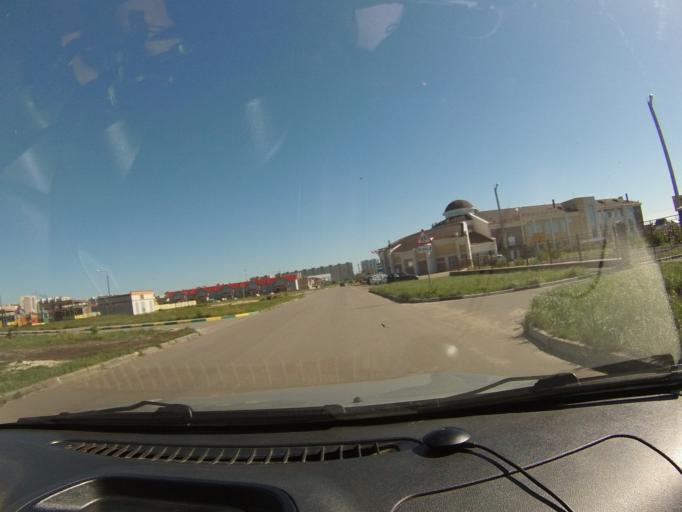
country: RU
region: Tambov
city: Tambov
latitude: 52.7708
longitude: 41.3833
